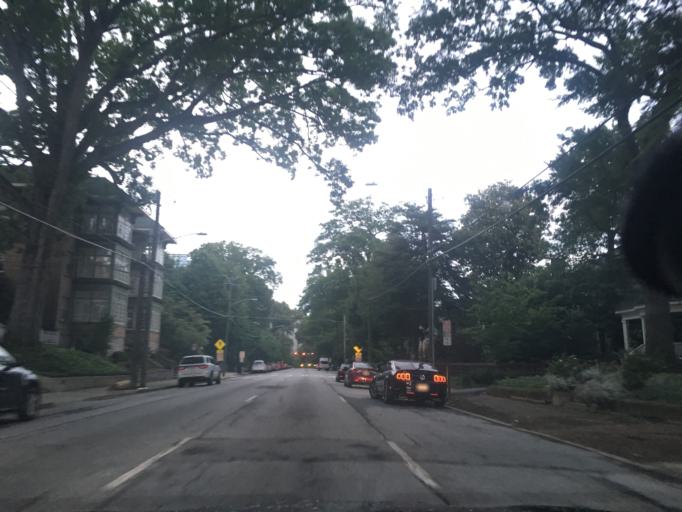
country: US
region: Georgia
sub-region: Fulton County
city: Atlanta
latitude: 33.7765
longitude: -84.3814
